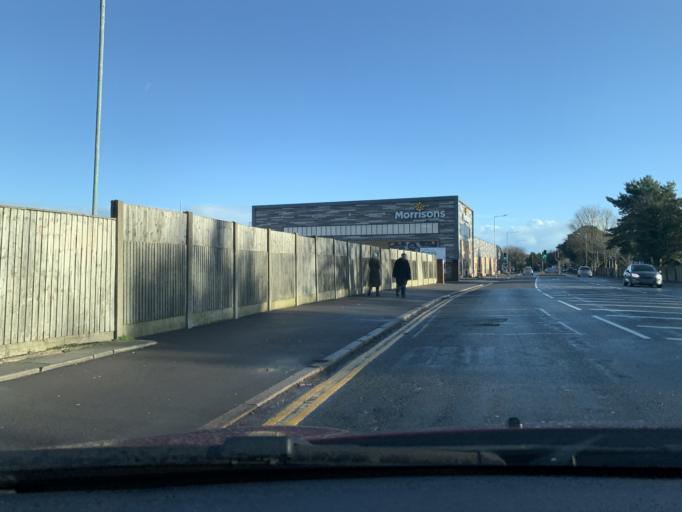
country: GB
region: England
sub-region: Kent
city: Folkestone
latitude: 51.0853
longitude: 1.1594
